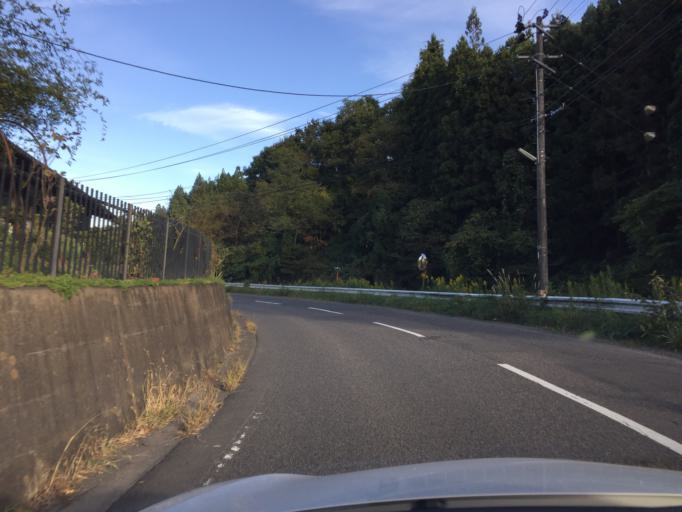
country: JP
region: Fukushima
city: Ishikawa
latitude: 37.1851
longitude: 140.5577
